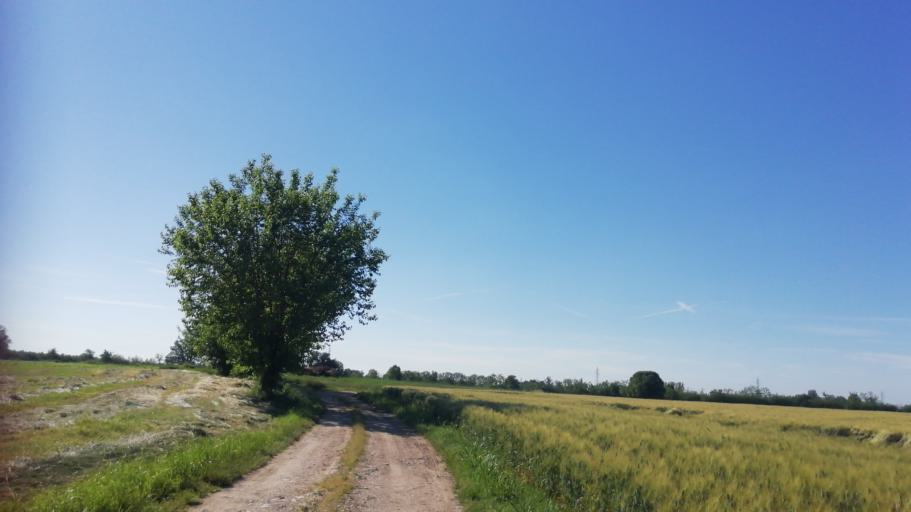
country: IT
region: Emilia-Romagna
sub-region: Provincia di Piacenza
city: Borgonovo Valtidone
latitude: 44.9929
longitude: 9.4669
